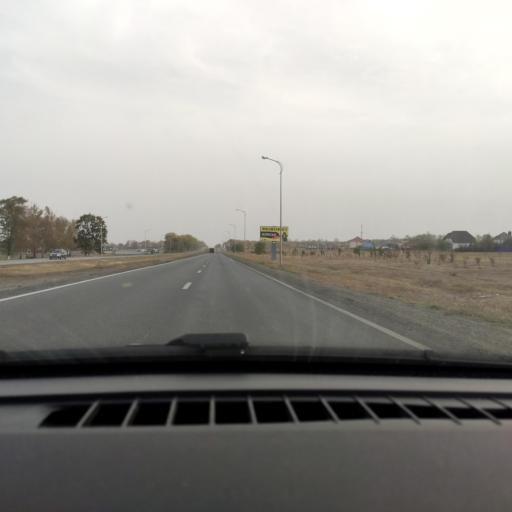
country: RU
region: Belgorod
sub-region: Belgorodskiy Rayon
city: Belgorod
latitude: 50.6549
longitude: 36.6925
